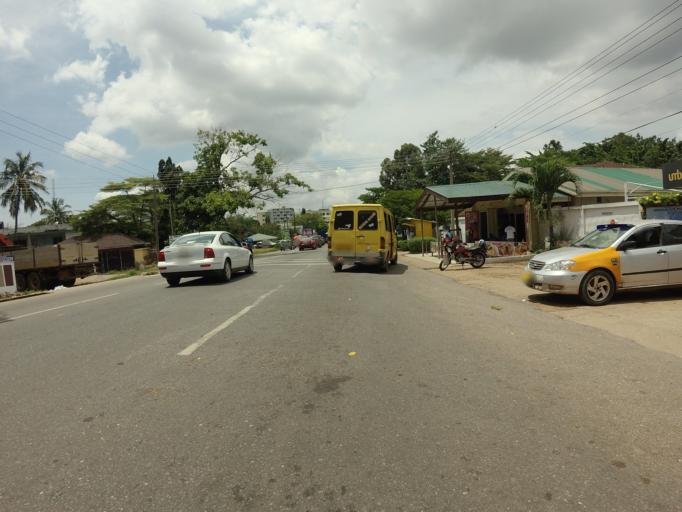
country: GH
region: Greater Accra
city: Medina Estates
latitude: 5.6301
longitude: -0.1746
